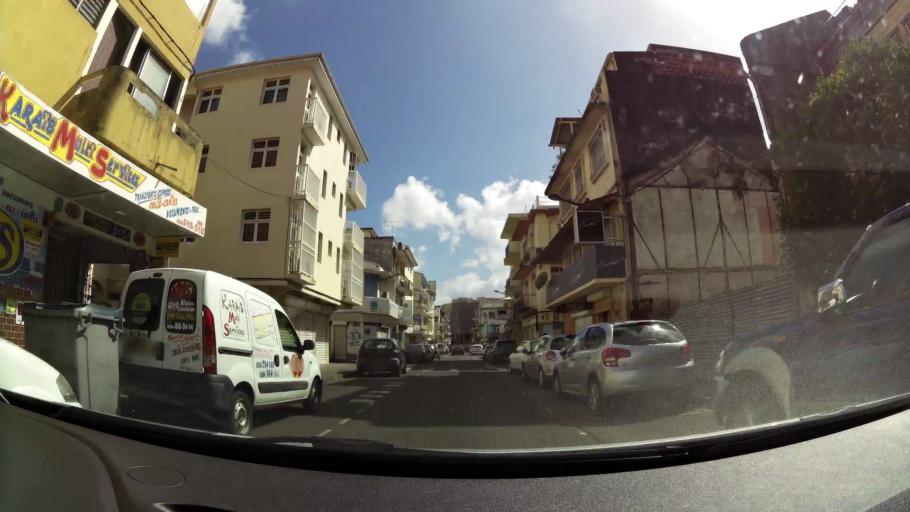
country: MQ
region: Martinique
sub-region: Martinique
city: Fort-de-France
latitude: 14.6098
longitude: -61.0706
